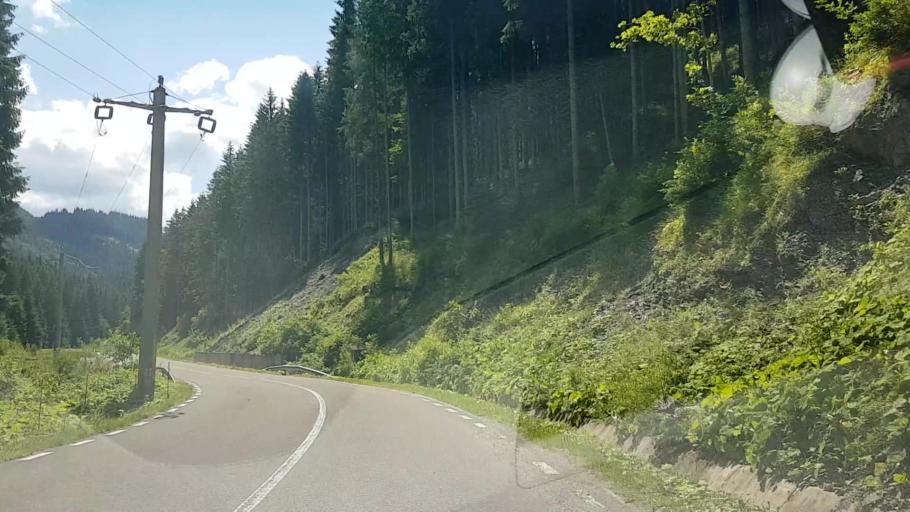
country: RO
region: Suceava
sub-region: Comuna Sadova
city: Sadova
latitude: 47.4762
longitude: 25.4990
